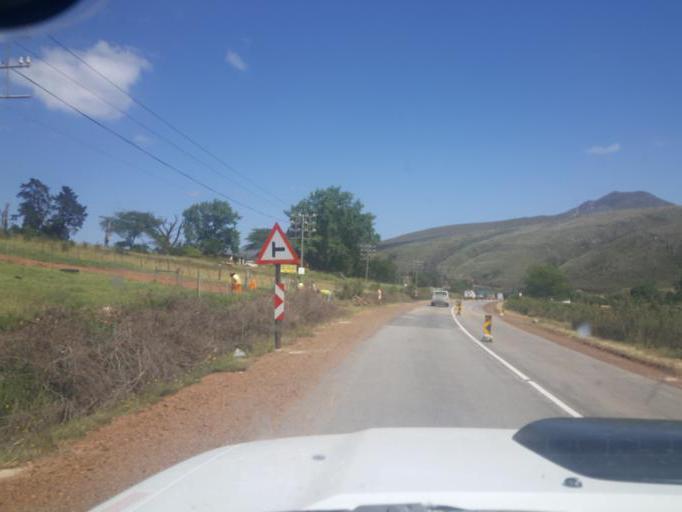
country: ZA
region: Eastern Cape
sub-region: Cacadu District Municipality
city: Kareedouw
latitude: -33.9468
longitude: 24.3177
